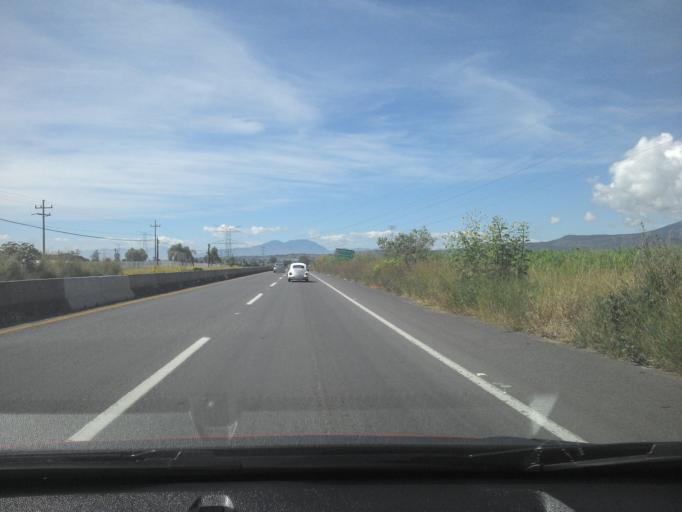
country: MX
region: Jalisco
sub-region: Tala
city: Los Ruisenores
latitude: 20.7127
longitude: -103.6563
